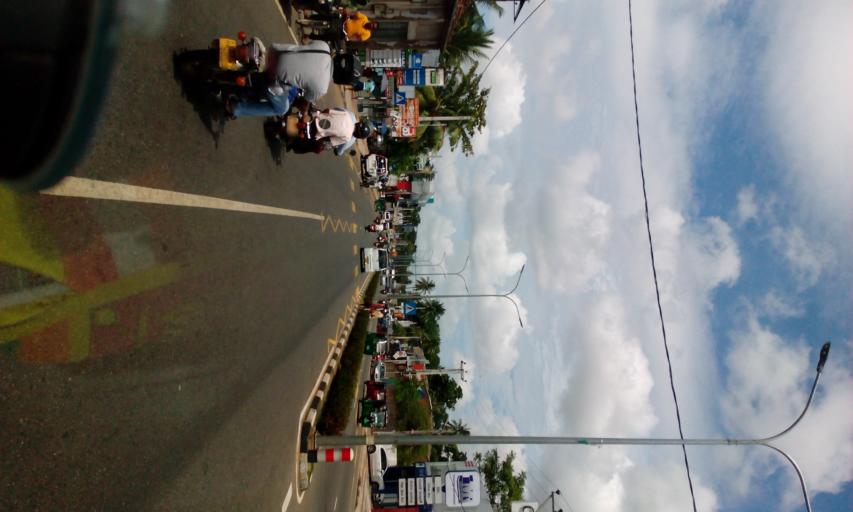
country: LK
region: North Western
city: Kuliyapitiya
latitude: 7.4685
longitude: 80.0371
